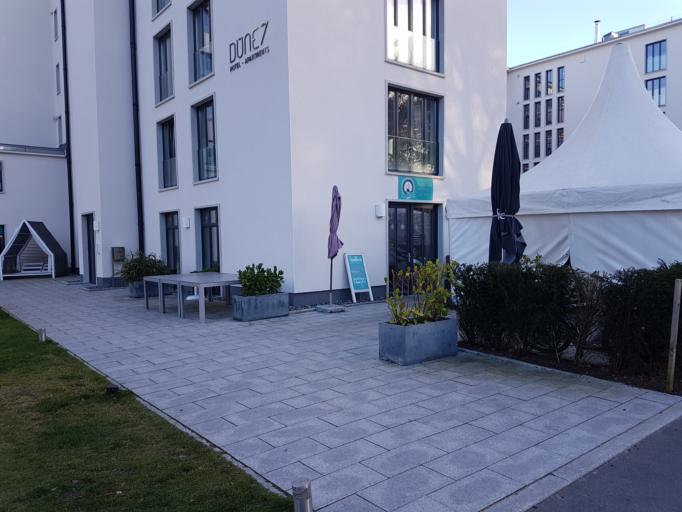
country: DE
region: Mecklenburg-Vorpommern
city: Ostseebad Binz
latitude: 54.4322
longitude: 13.5794
